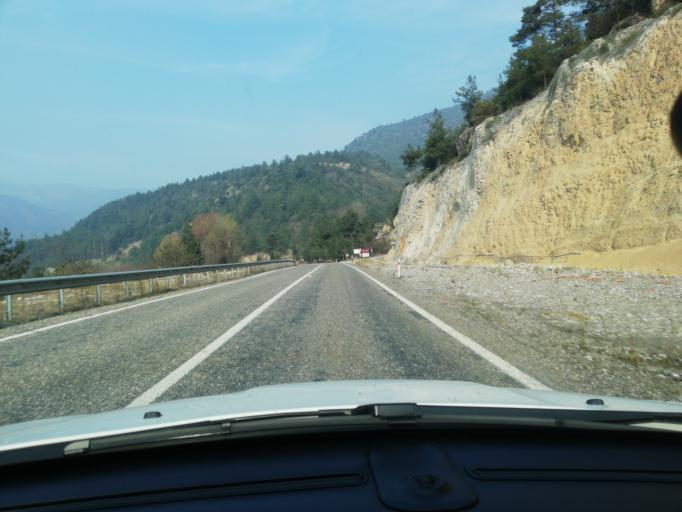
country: TR
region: Karabuk
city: Karabuk
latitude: 41.1586
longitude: 32.5494
